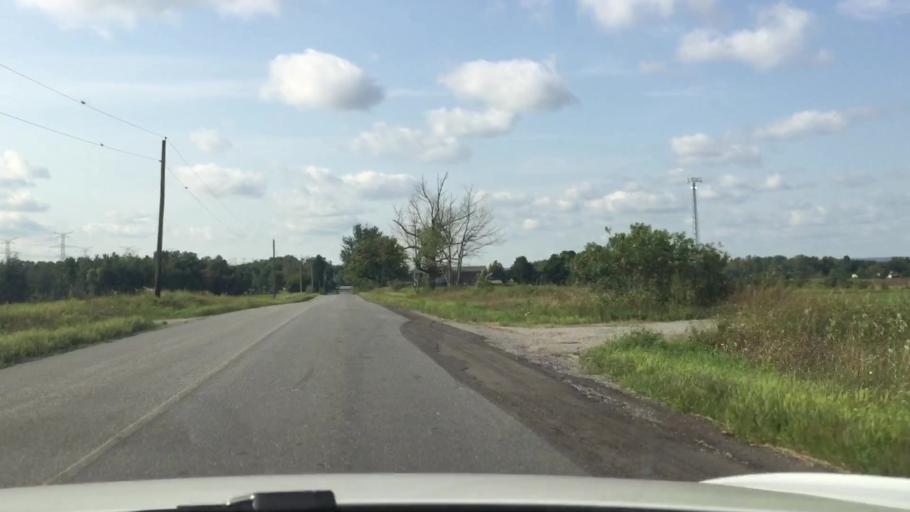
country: CA
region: Ontario
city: Oshawa
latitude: 43.9538
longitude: -78.7539
